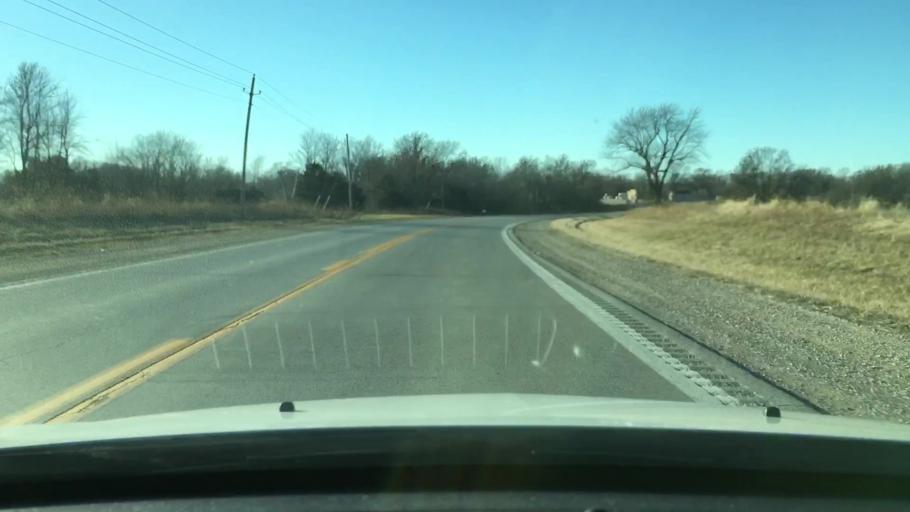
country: US
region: Missouri
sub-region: Audrain County
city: Mexico
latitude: 39.1888
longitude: -91.9764
